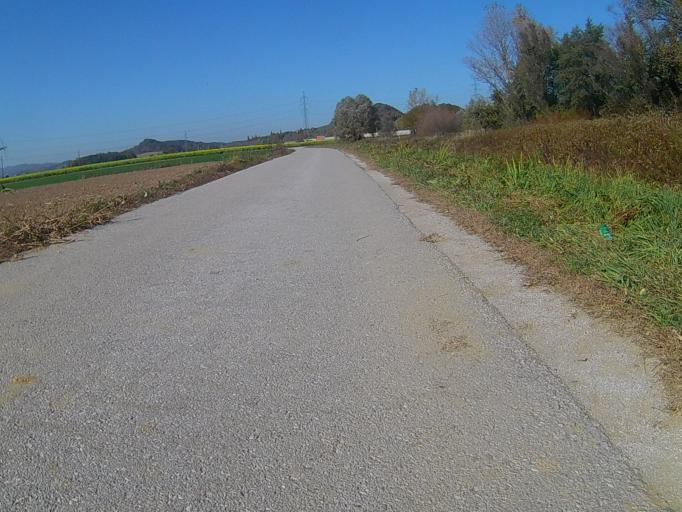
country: SI
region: Pesnica
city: Pesnica pri Mariboru
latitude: 46.5837
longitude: 15.7224
